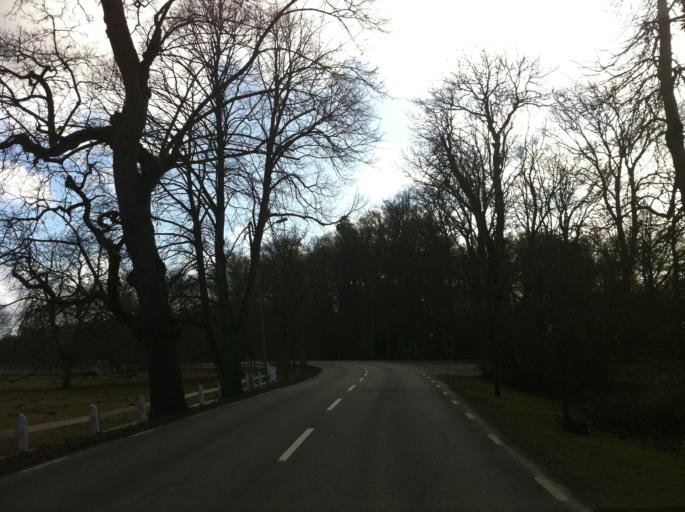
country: SE
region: Skane
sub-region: Bromolla Kommun
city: Bromoella
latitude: 56.0462
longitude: 14.4294
